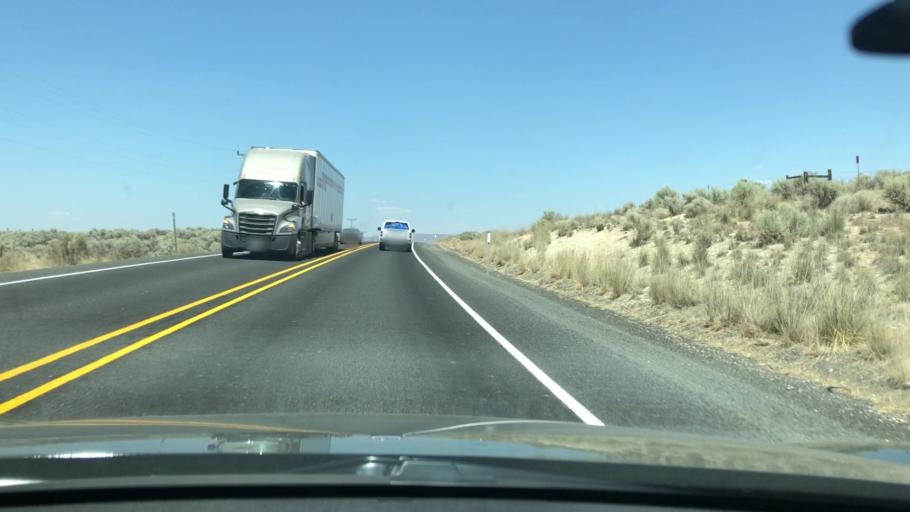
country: US
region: Idaho
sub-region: Owyhee County
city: Murphy
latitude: 42.9977
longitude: -117.0620
